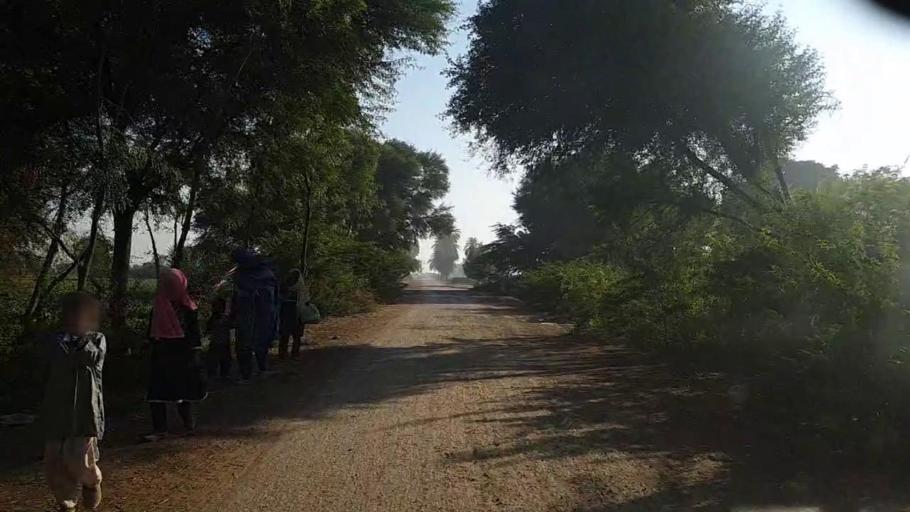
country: PK
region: Sindh
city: Darya Khan Marri
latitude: 26.6954
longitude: 68.3625
